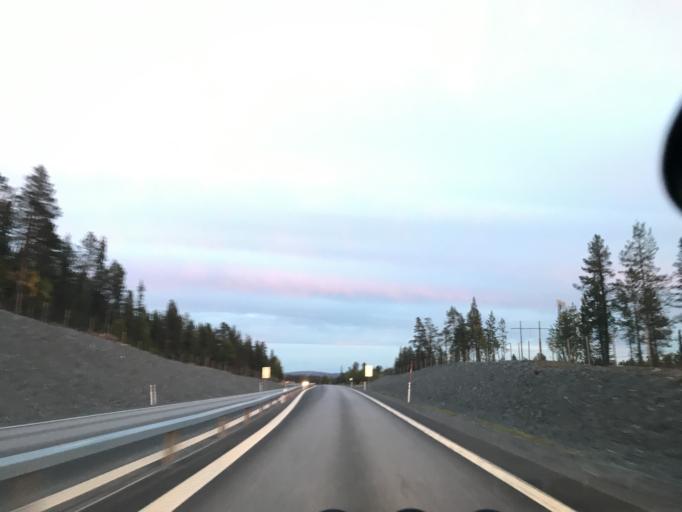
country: SE
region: Norrbotten
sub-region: Gallivare Kommun
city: Malmberget
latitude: 67.6780
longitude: 20.8866
